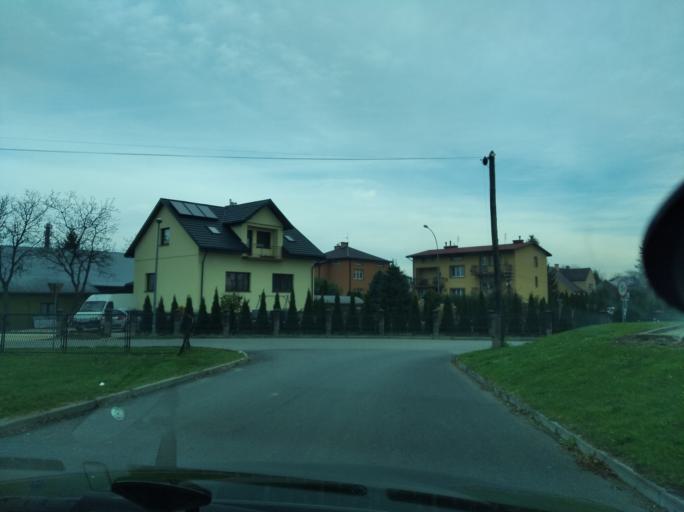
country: PL
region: Subcarpathian Voivodeship
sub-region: Powiat przeworski
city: Przeworsk
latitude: 50.0618
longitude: 22.4739
